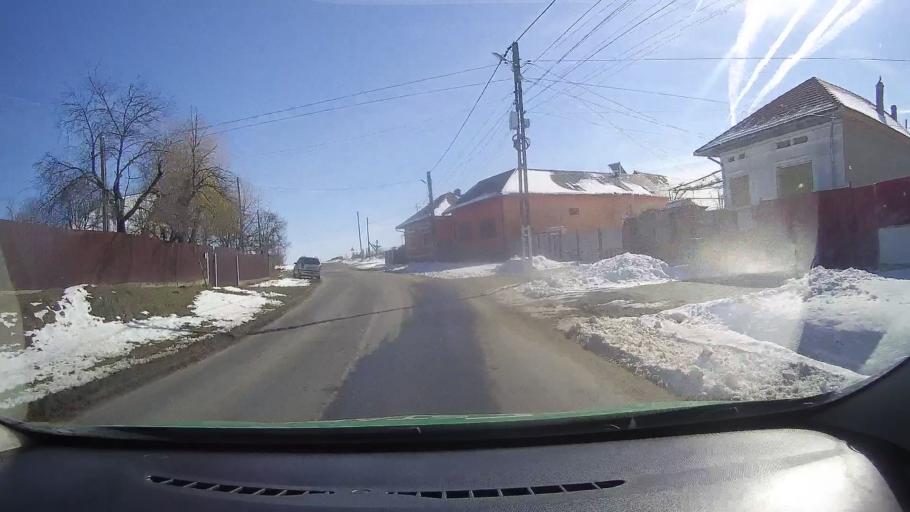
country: RO
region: Brasov
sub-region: Comuna Lisa
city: Lisa
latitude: 45.7240
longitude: 24.8539
